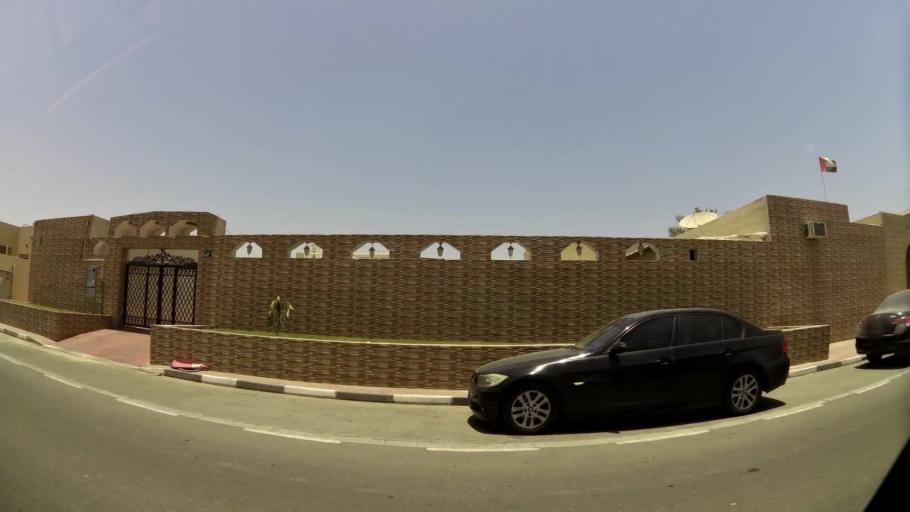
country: AE
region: Ash Shariqah
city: Sharjah
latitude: 25.2333
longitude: 55.2857
